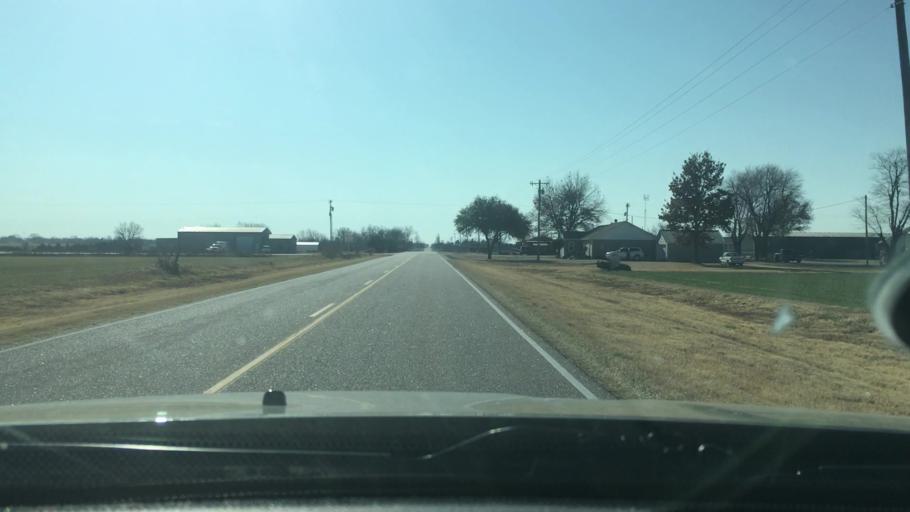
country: US
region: Oklahoma
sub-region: Garvin County
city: Stratford
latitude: 34.8125
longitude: -96.9677
